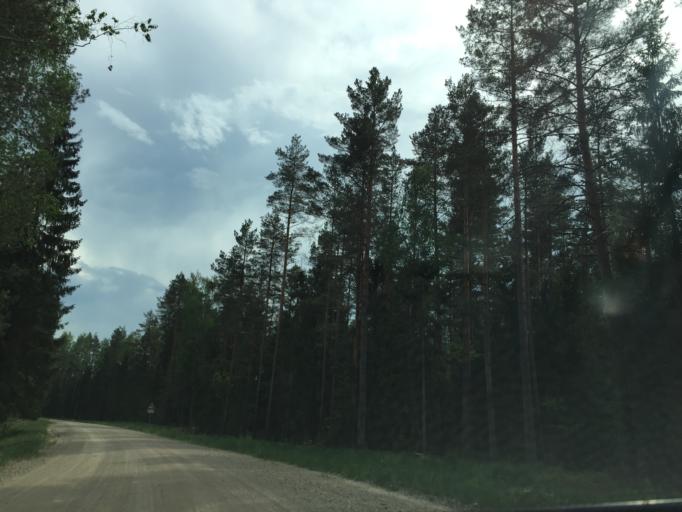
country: LV
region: Livani
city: Livani
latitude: 56.5682
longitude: 26.2133
